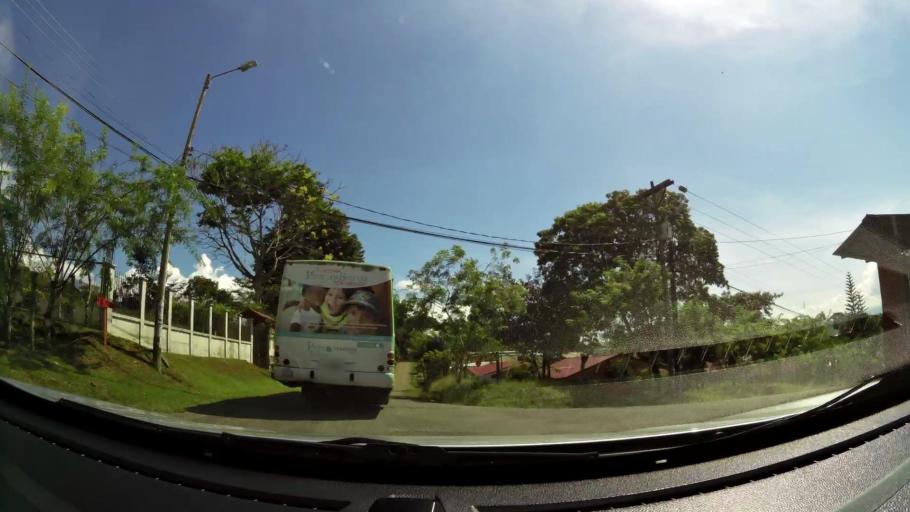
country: CR
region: San Jose
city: San Isidro
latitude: 9.3862
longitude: -83.6980
